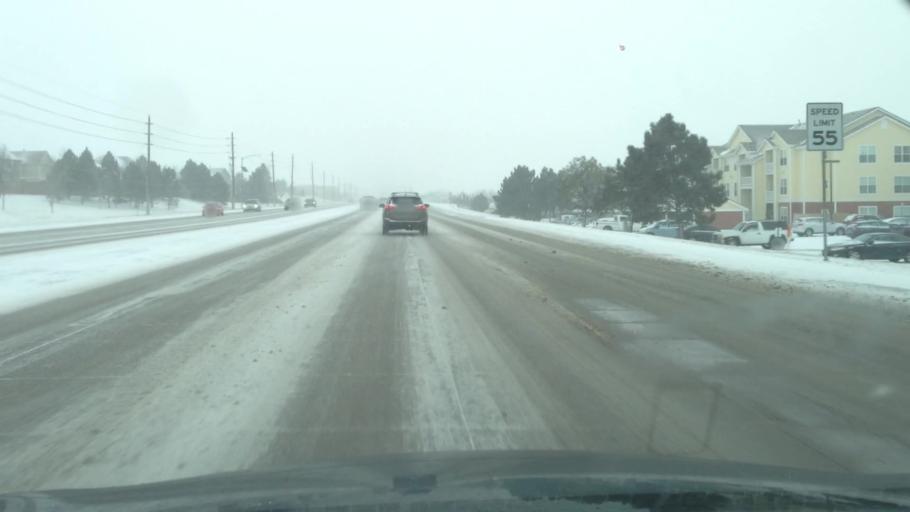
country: US
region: Colorado
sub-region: Arapahoe County
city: Dove Valley
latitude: 39.6090
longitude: -104.8104
